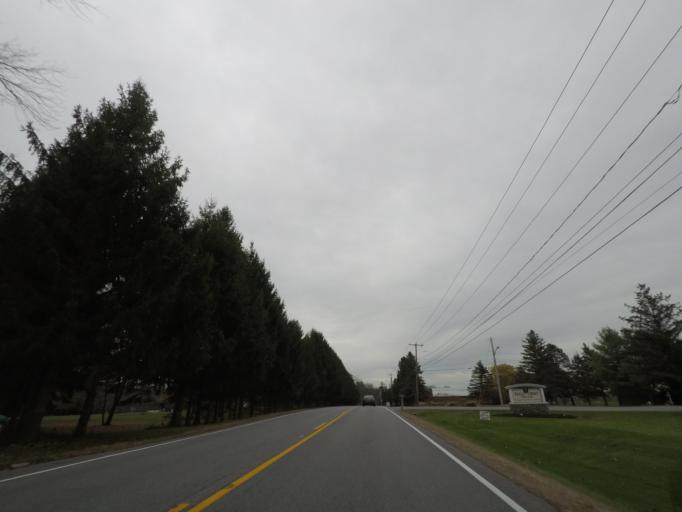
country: US
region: New York
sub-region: Saratoga County
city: Country Knolls
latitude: 42.8930
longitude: -73.8547
